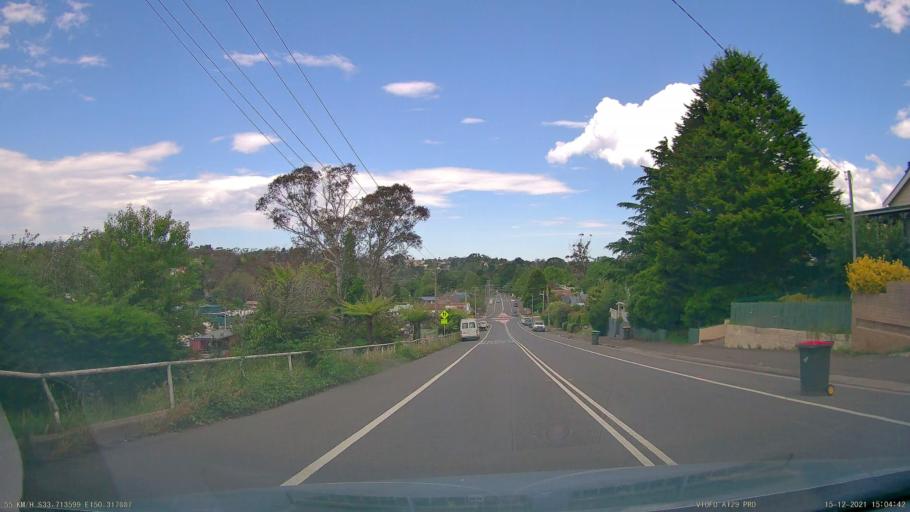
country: AU
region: New South Wales
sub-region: Blue Mountains Municipality
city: Katoomba
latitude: -33.7136
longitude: 150.3180
